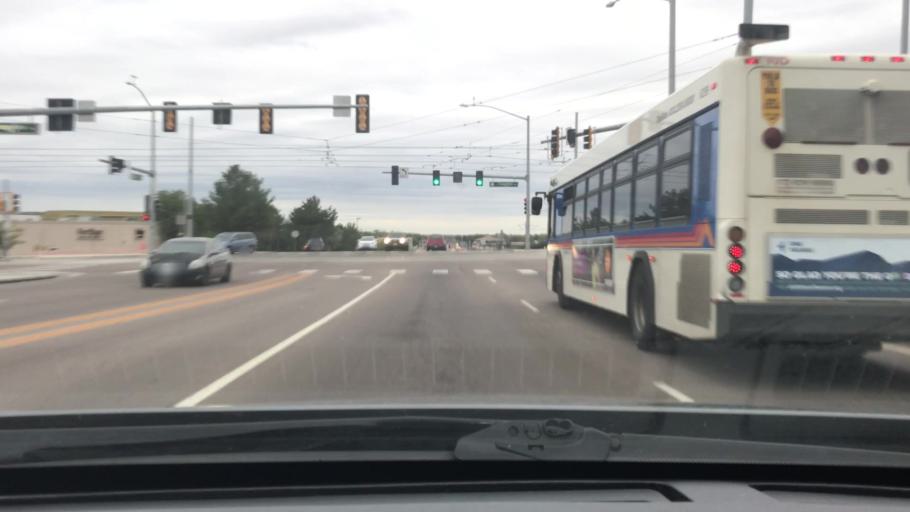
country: US
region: Colorado
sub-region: Adams County
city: Aurora
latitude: 39.7035
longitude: -104.8192
